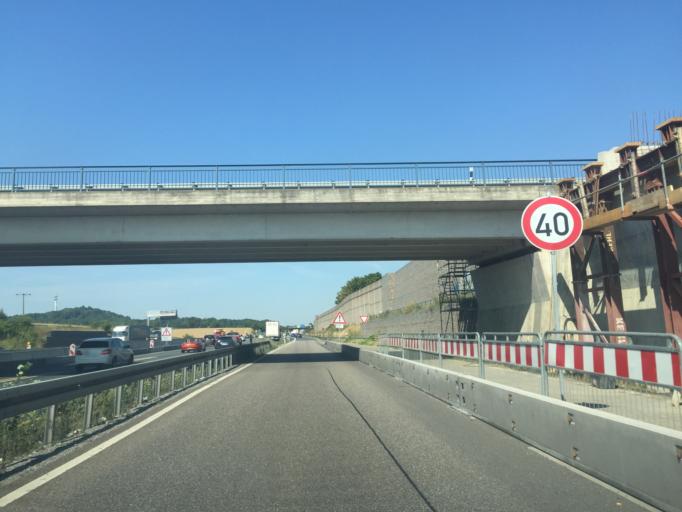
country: DE
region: Baden-Wuerttemberg
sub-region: Karlsruhe Region
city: Sinsheim
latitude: 49.2439
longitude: 8.8770
